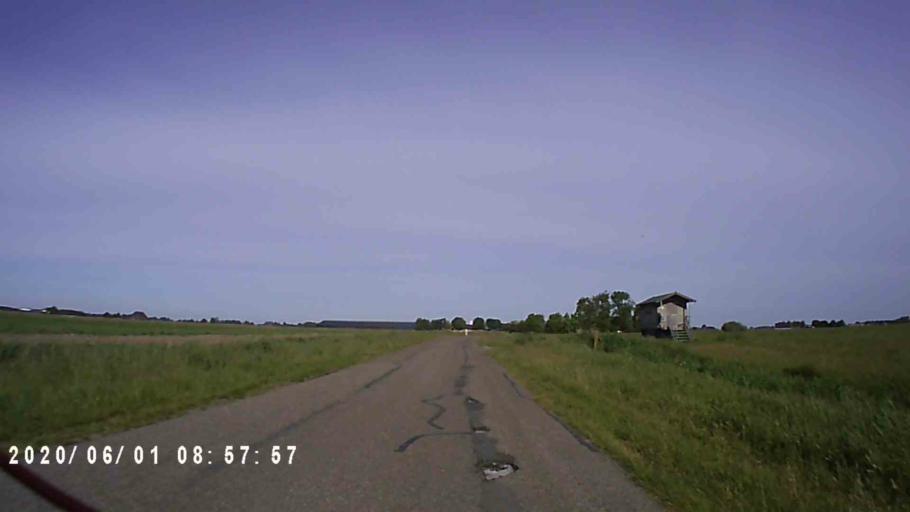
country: NL
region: Friesland
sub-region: Gemeente Leeuwarderadeel
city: Britsum
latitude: 53.2812
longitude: 5.8093
